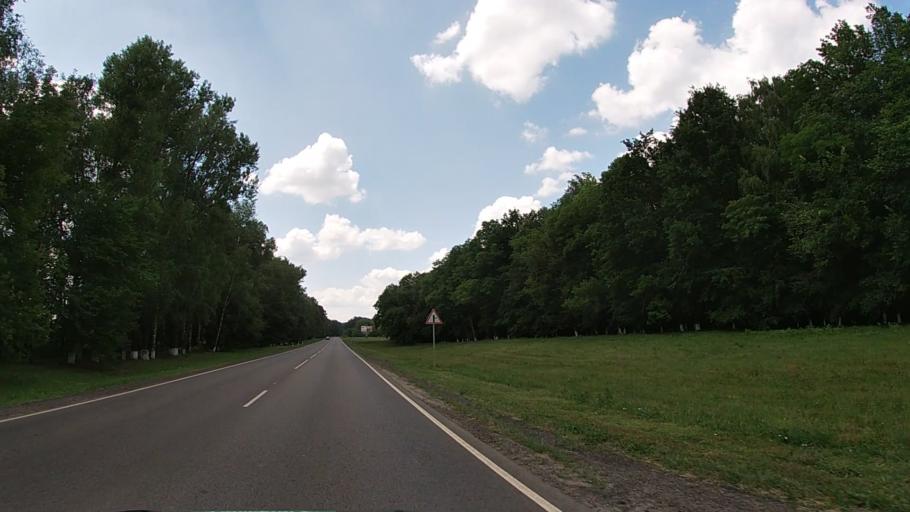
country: RU
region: Belgorod
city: Grayvoron
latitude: 50.4984
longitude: 35.7186
